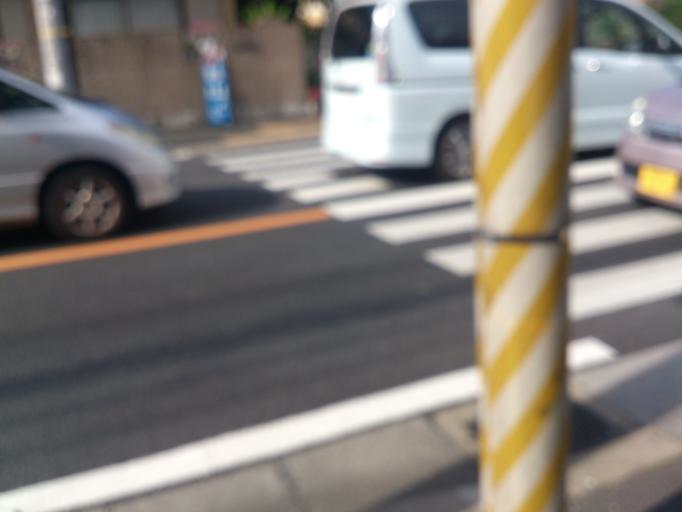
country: JP
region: Chiba
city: Matsudo
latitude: 35.7906
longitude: 139.9296
